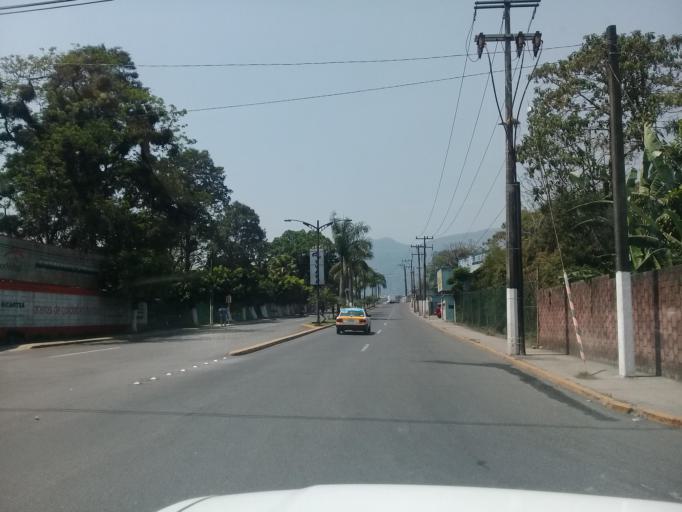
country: MX
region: Veracruz
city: Ixtac Zoquitlan
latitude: 18.8625
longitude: -97.0487
